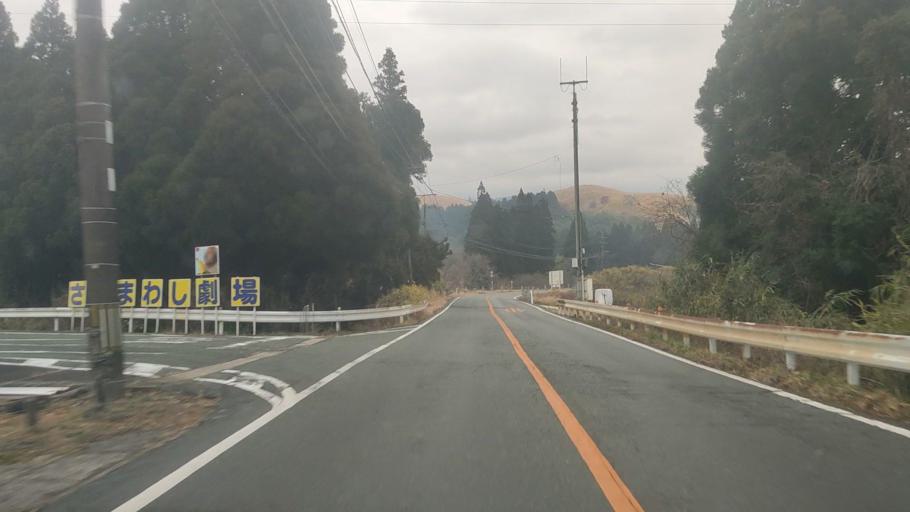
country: JP
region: Kumamoto
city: Aso
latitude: 32.9009
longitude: 130.9975
